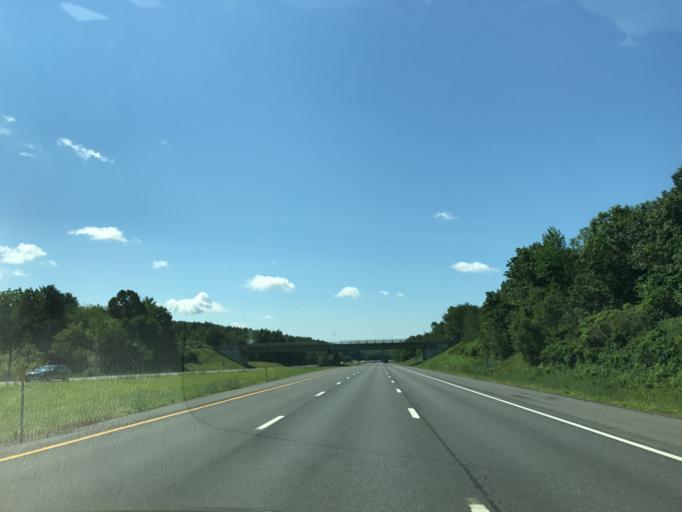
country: US
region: New York
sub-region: Rensselaer County
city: East Greenbush
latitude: 42.6027
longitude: -73.6829
